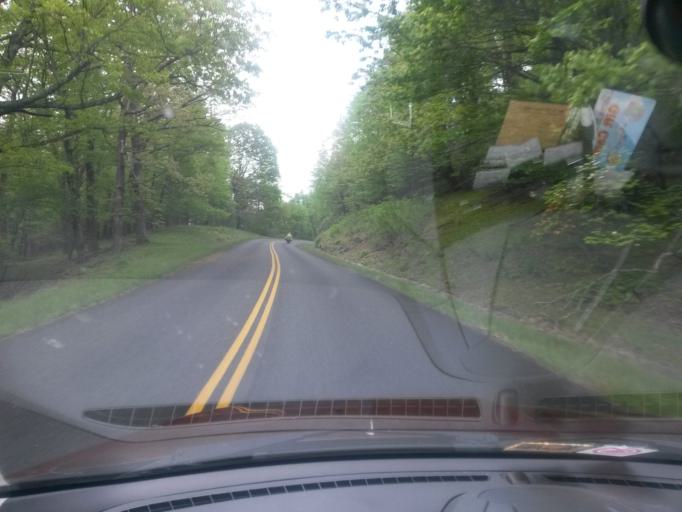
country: US
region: Virginia
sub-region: Floyd County
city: Floyd
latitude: 36.8192
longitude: -80.3445
